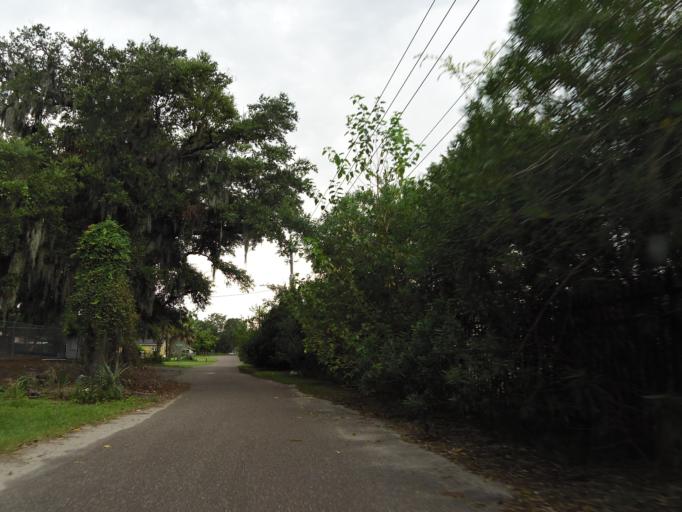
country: US
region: Florida
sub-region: Duval County
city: Jacksonville
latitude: 30.3510
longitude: -81.6286
